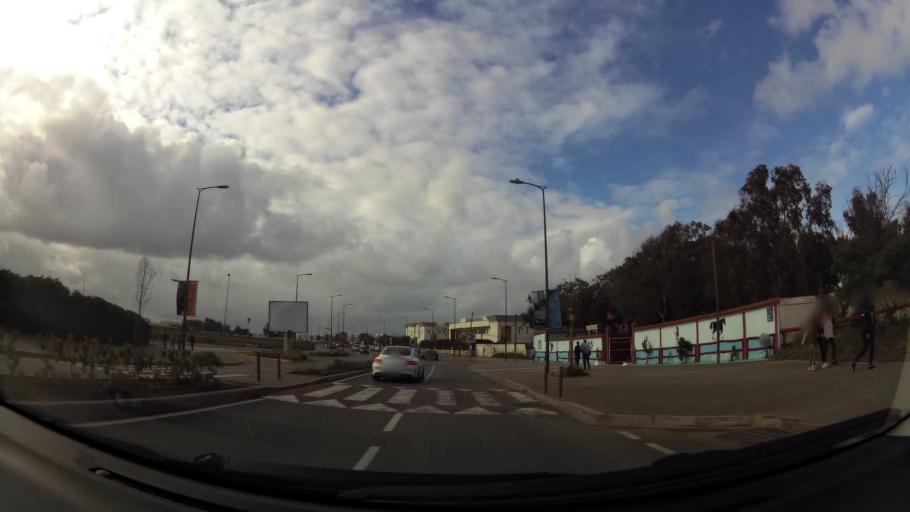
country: MA
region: Grand Casablanca
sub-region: Casablanca
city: Casablanca
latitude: 33.5732
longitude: -7.7004
